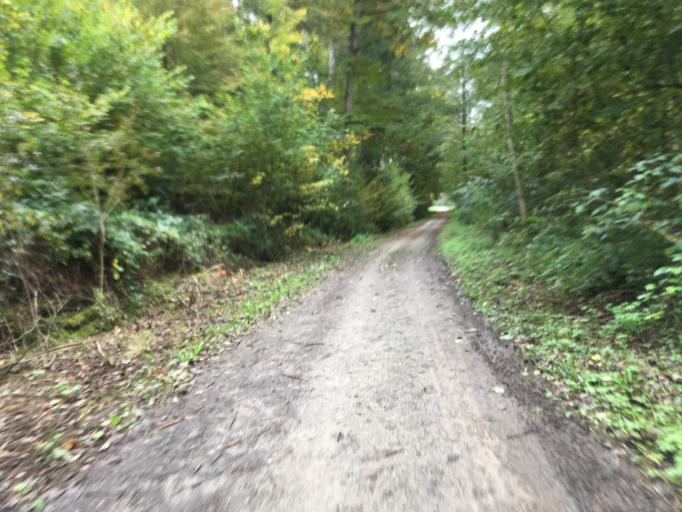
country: DE
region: Baden-Wuerttemberg
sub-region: Tuebingen Region
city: Gomaringen
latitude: 48.4820
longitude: 9.0772
